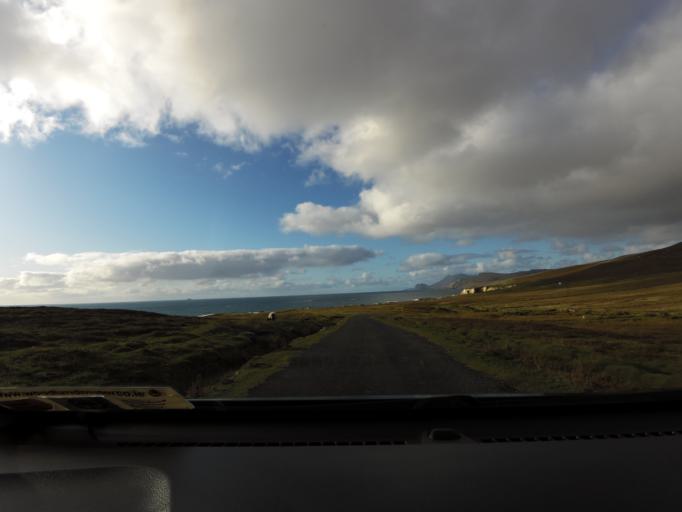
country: IE
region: Connaught
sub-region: Maigh Eo
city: Belmullet
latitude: 53.8886
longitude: -9.9846
